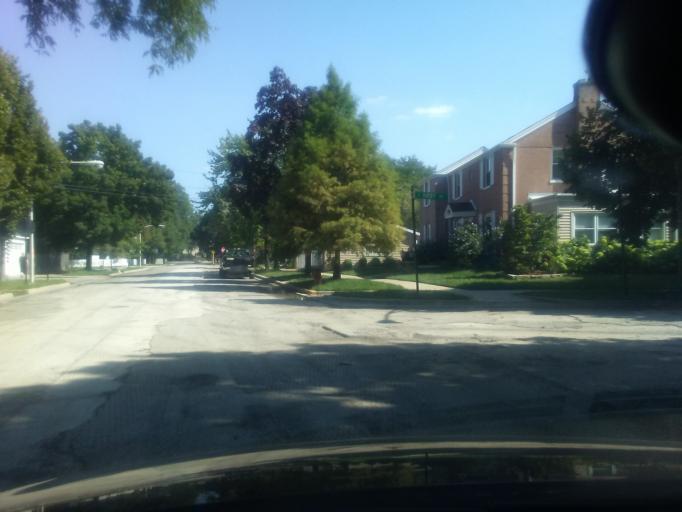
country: US
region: Illinois
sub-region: Cook County
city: Lincolnwood
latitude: 41.9862
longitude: -87.7429
